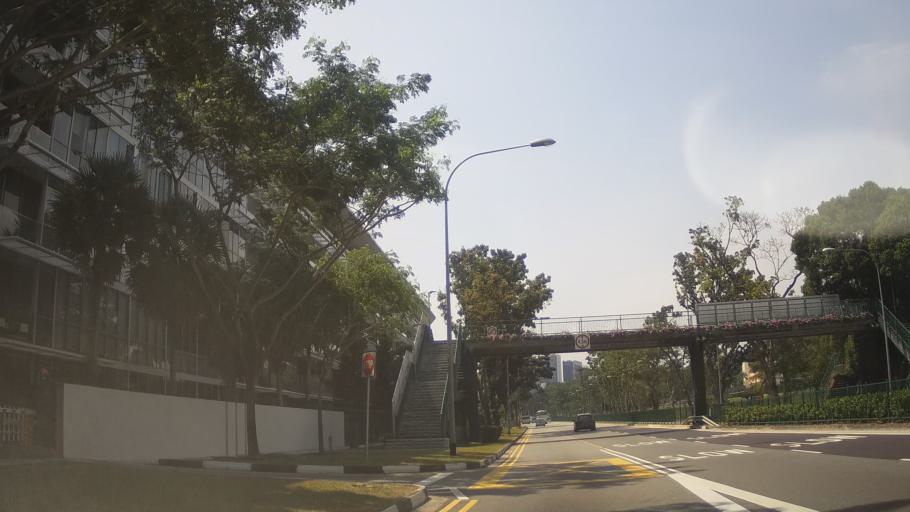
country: MY
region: Johor
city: Johor Bahru
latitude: 1.3753
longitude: 103.7627
